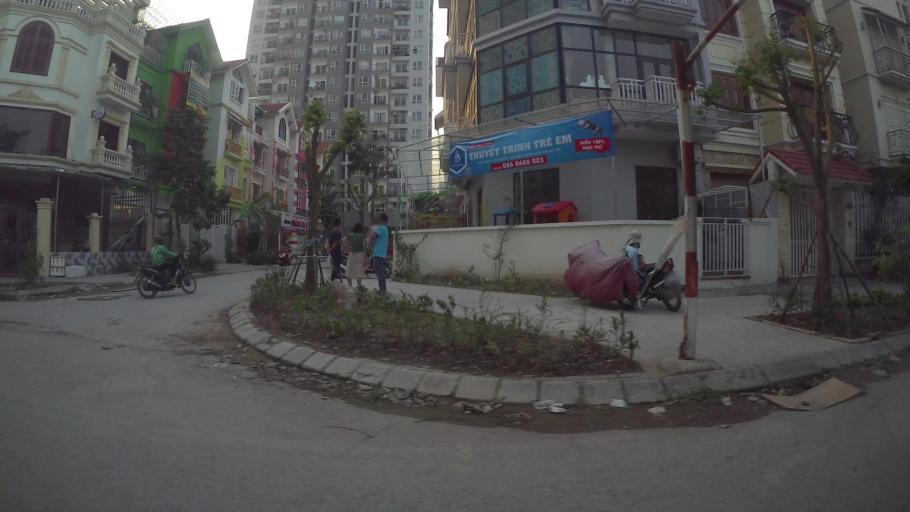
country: VN
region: Ha Noi
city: Thanh Xuan
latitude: 20.9744
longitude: 105.8204
